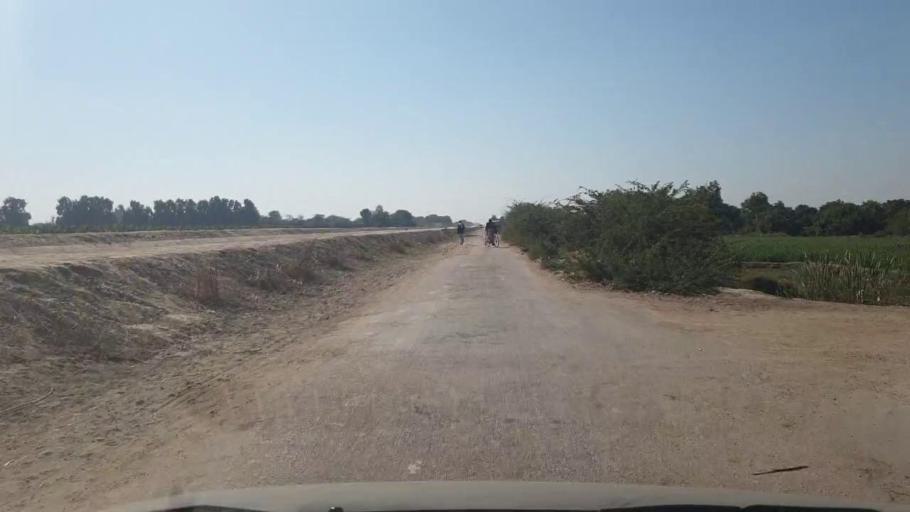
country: PK
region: Sindh
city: Mirwah Gorchani
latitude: 25.3009
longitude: 69.1029
